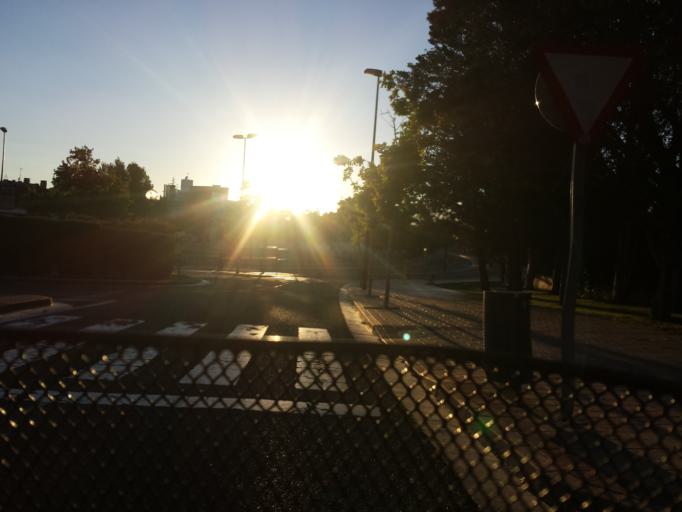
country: ES
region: Aragon
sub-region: Provincia de Zaragoza
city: Montecanal
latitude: 41.6305
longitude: -0.9361
